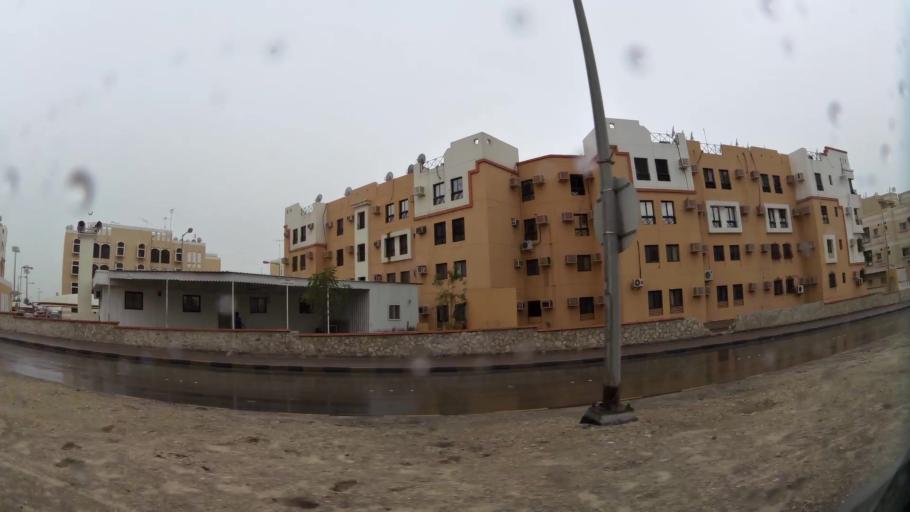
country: BH
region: Northern
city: Madinat `Isa
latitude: 26.1773
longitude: 50.5513
